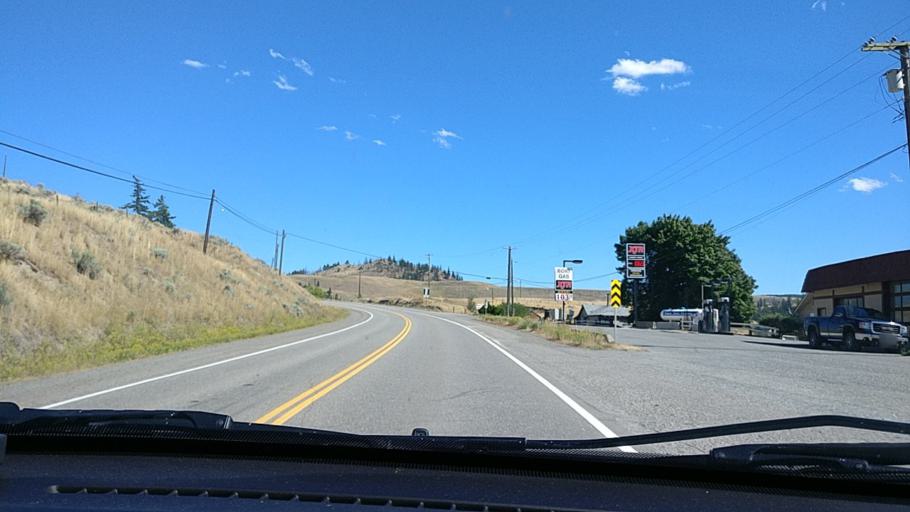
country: CA
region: British Columbia
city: Kamloops
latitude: 50.6635
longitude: -120.5553
